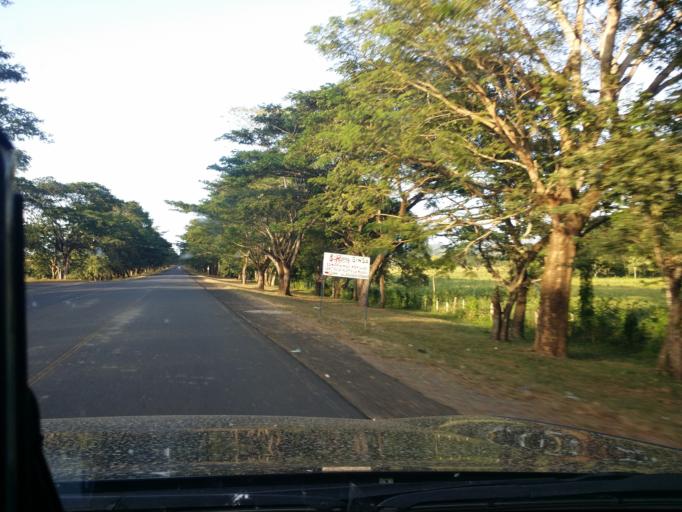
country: NI
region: Rio San Juan
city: San Miguelito
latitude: 11.4411
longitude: -84.8518
